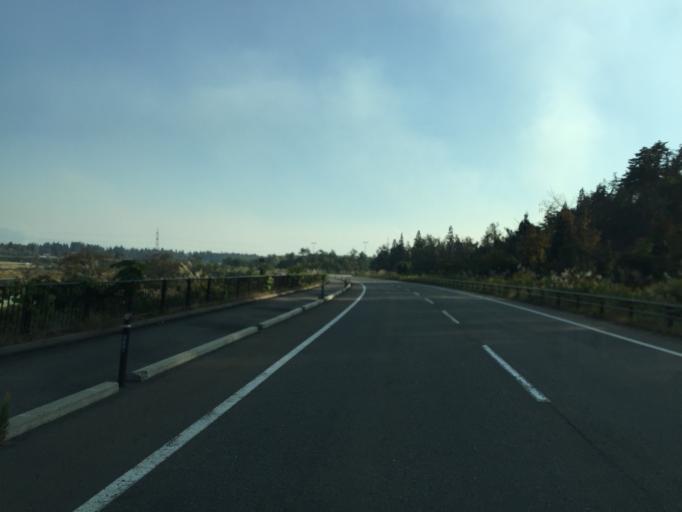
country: JP
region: Fukushima
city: Kitakata
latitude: 37.7089
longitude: 139.8675
